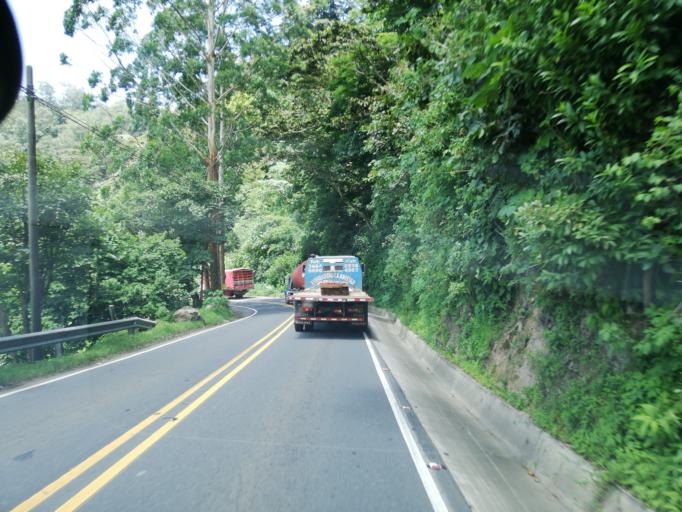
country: CR
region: Alajuela
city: Zarcero
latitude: 10.2237
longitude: -84.4047
